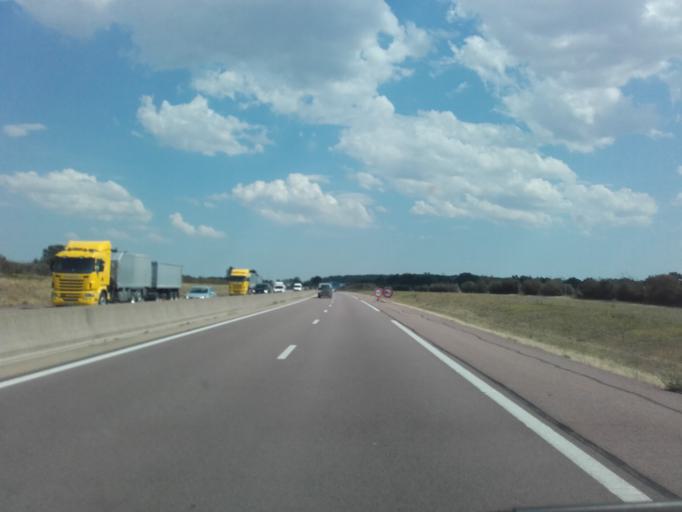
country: FR
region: Bourgogne
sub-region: Departement de l'Yonne
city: Avallon
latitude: 47.5058
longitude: 4.0126
